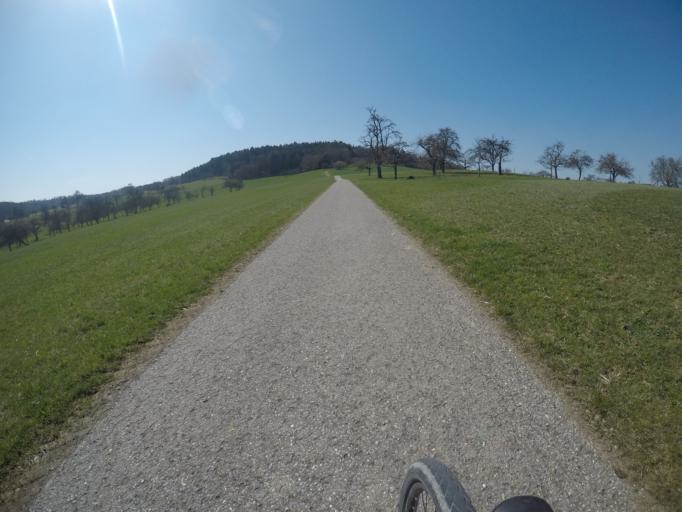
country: DE
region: Baden-Wuerttemberg
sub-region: Karlsruhe Region
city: Gechingen
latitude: 48.6927
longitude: 8.8108
